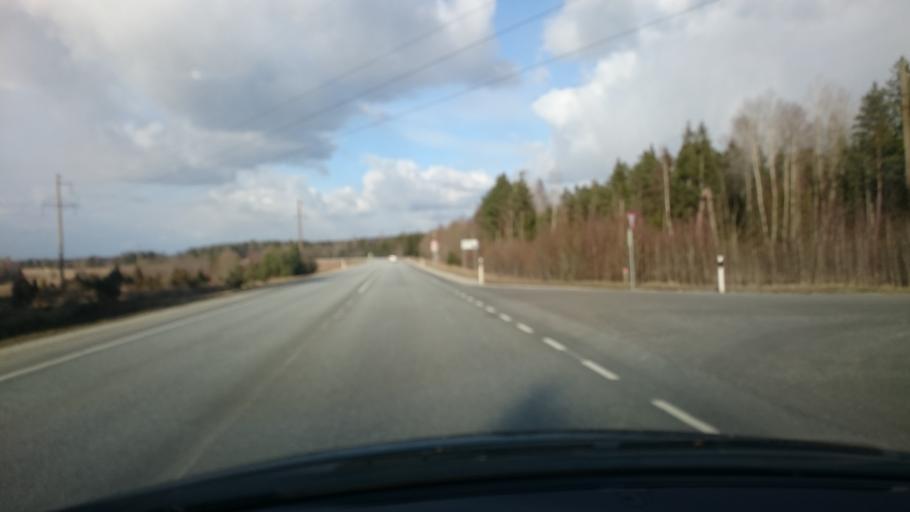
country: EE
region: Harju
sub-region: Nissi vald
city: Riisipere
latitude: 59.1306
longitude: 24.3213
